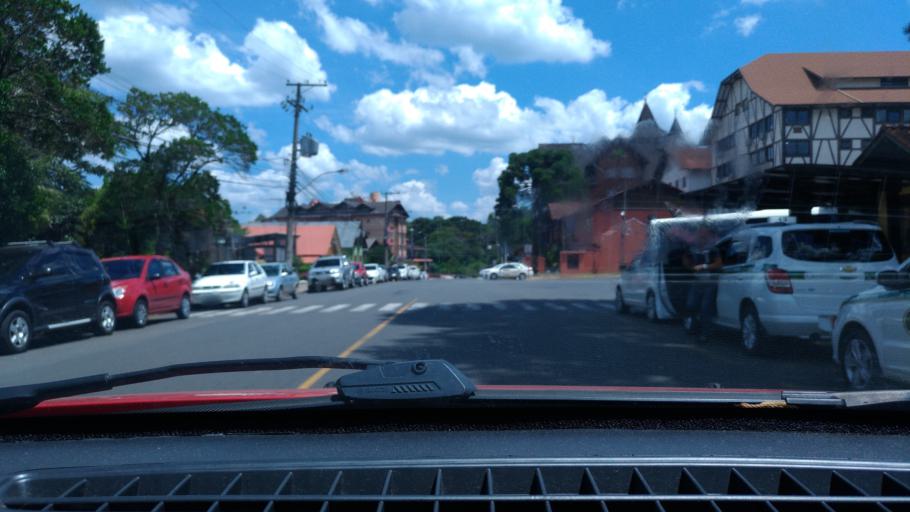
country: BR
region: Rio Grande do Sul
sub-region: Canela
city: Canela
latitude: -29.3835
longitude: -50.8716
